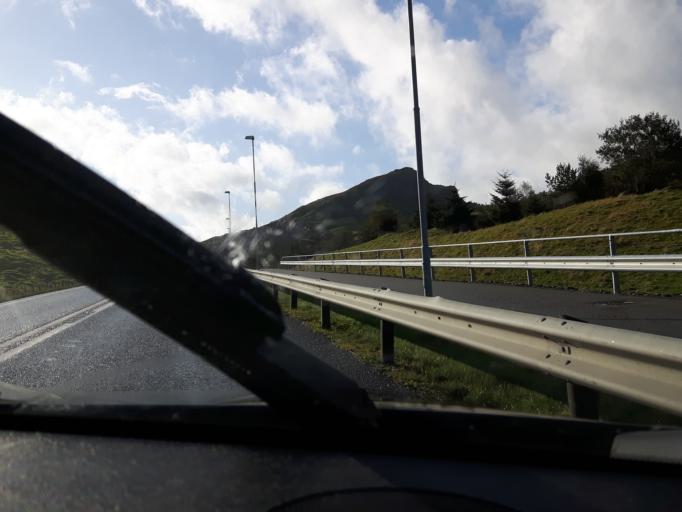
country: NO
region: Rogaland
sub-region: Gjesdal
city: Algard
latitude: 58.7607
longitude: 5.9005
